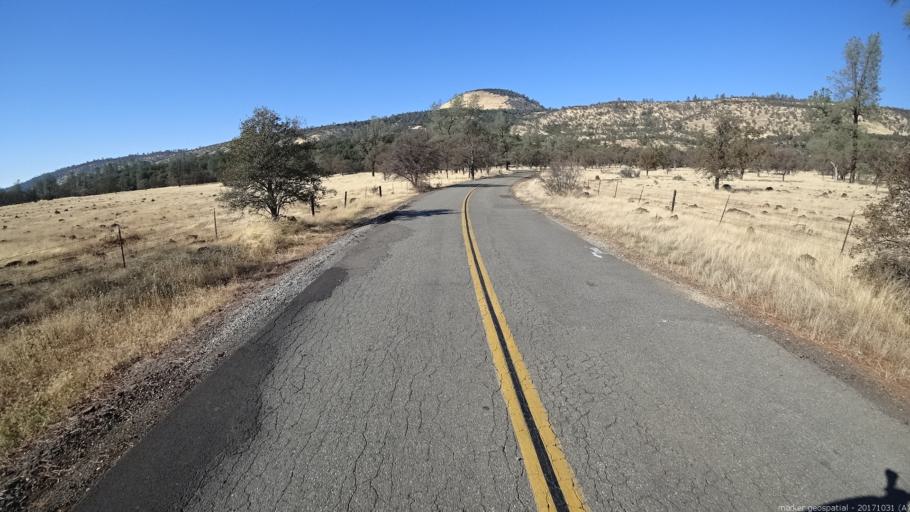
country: US
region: California
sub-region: Shasta County
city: Shingletown
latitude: 40.4370
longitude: -121.9836
